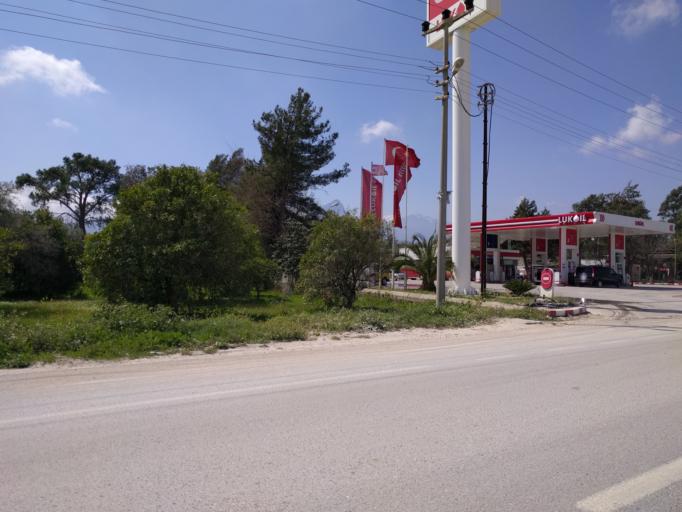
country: TR
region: Antalya
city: Cakirlar
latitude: 36.8941
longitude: 30.5996
